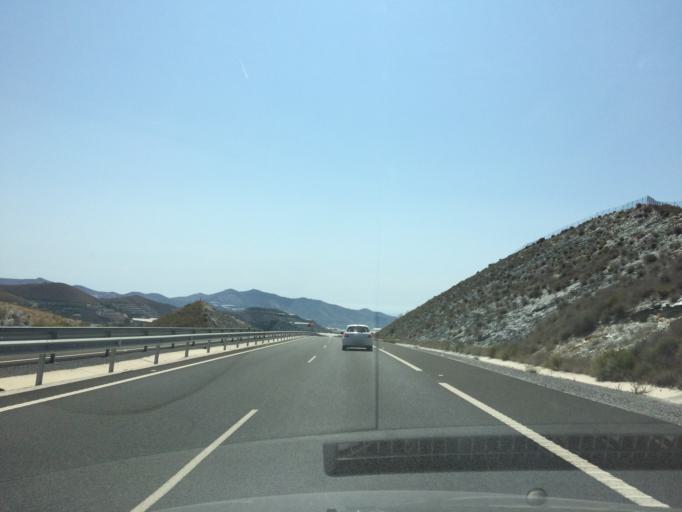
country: ES
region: Andalusia
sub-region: Provincia de Granada
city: Motril
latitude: 36.7609
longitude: -3.4852
